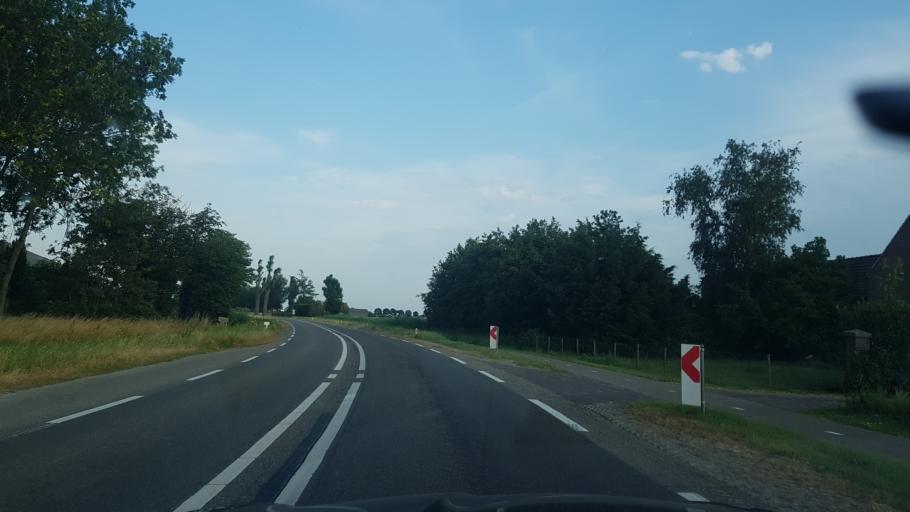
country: NL
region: Zeeland
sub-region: Gemeente Tholen
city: Tholen
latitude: 51.5388
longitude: 4.1742
